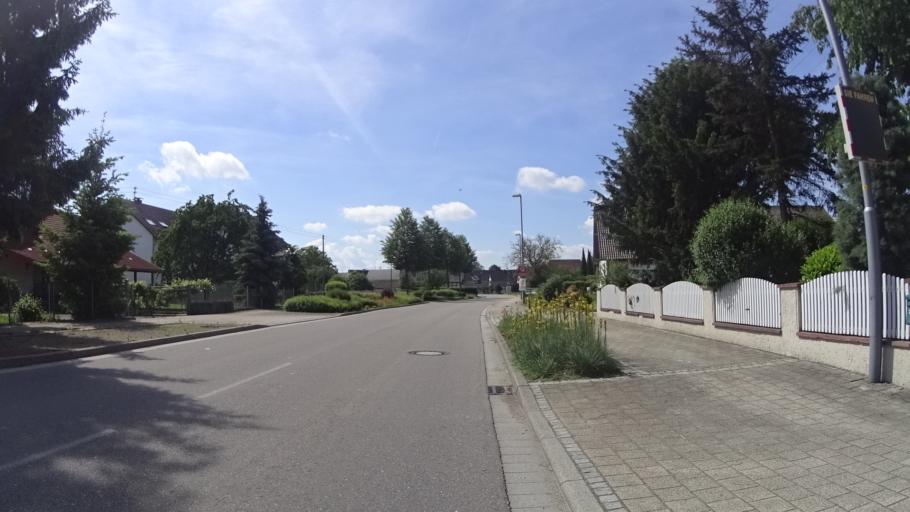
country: DE
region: Baden-Wuerttemberg
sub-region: Freiburg Region
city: Meissenheim
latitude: 48.4704
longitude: 7.8121
